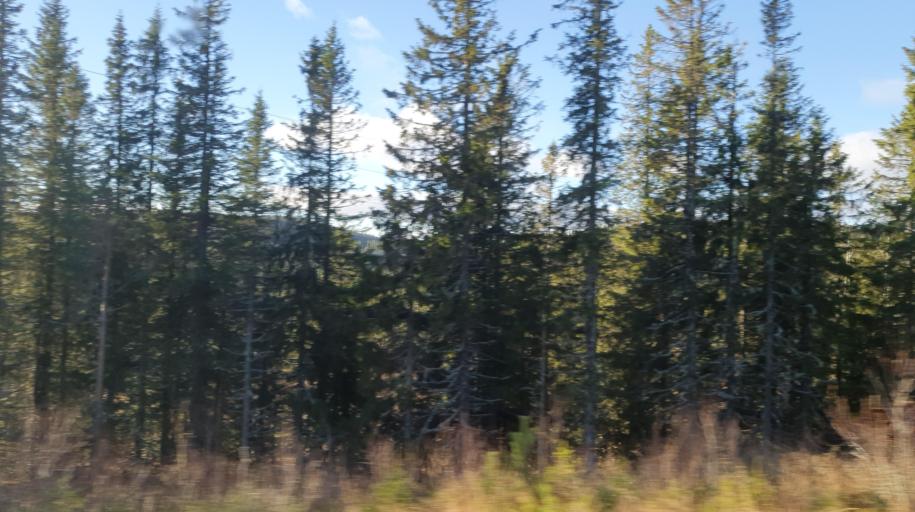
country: NO
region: Buskerud
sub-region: Krodsherad
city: Noresund
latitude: 60.2178
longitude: 9.5363
